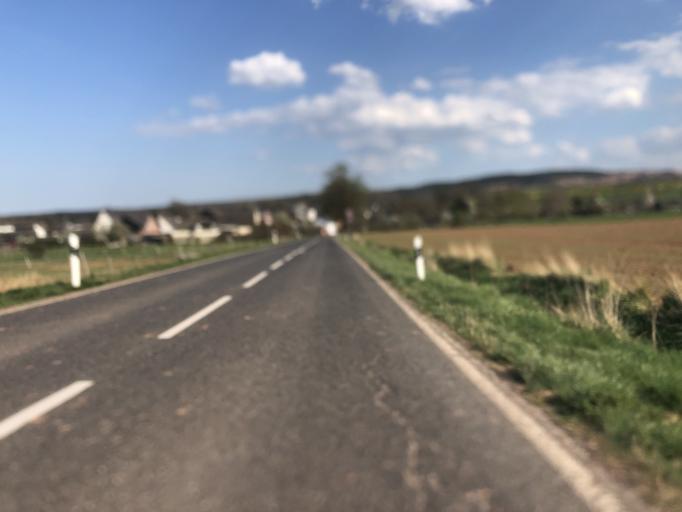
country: DE
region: North Rhine-Westphalia
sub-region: Regierungsbezirk Koln
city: Kall
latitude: 50.5865
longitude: 6.5806
